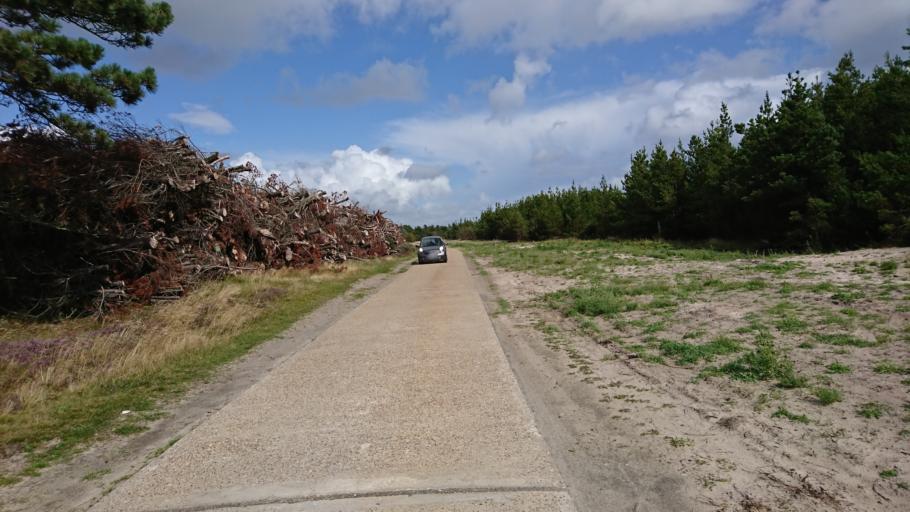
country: DK
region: South Denmark
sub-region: Fano Kommune
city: Nordby
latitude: 55.3881
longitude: 8.4189
